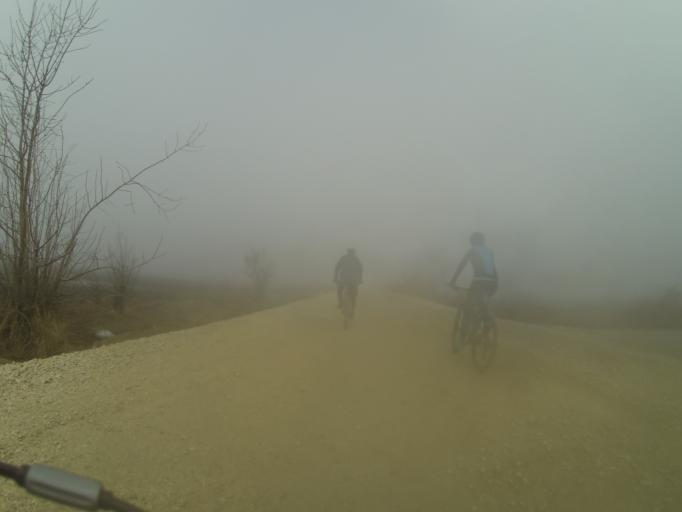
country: RO
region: Mehedinti
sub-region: Comuna Baclesu
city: Baclesu
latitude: 44.4606
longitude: 23.1150
